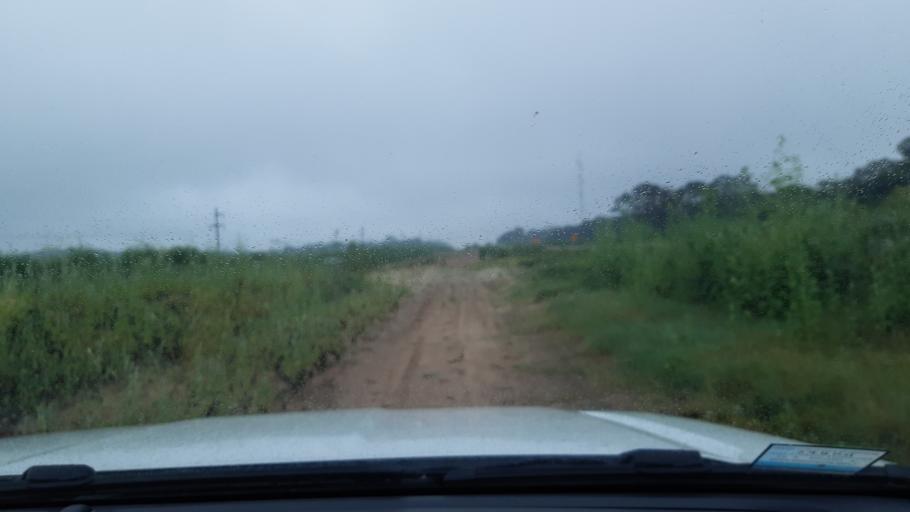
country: AR
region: Jujuy
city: La Mendieta
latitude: -24.3754
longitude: -65.0068
